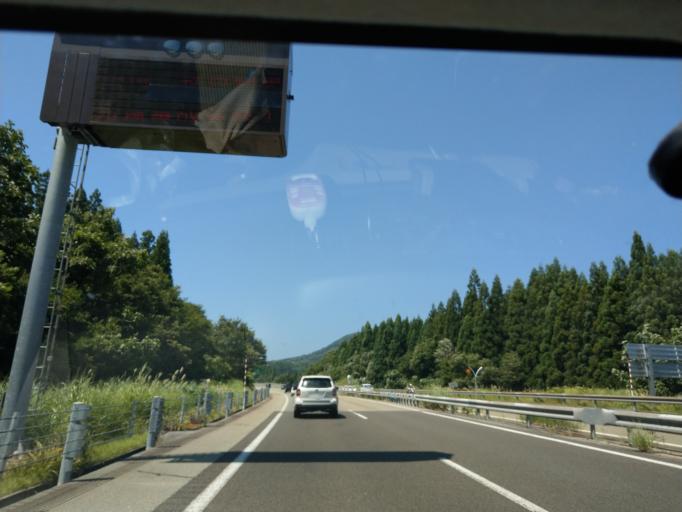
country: JP
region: Akita
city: Omagari
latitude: 39.4243
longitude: 140.4309
